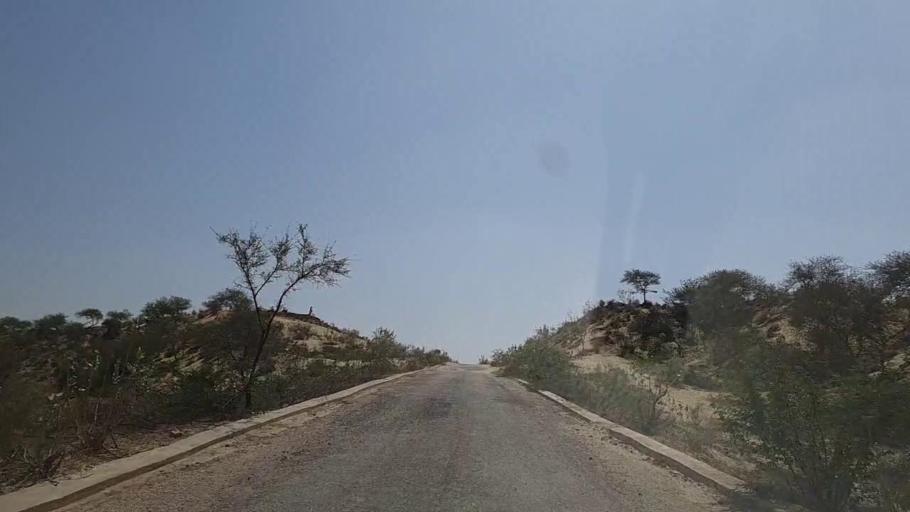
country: PK
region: Sindh
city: Diplo
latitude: 24.5063
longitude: 69.4242
